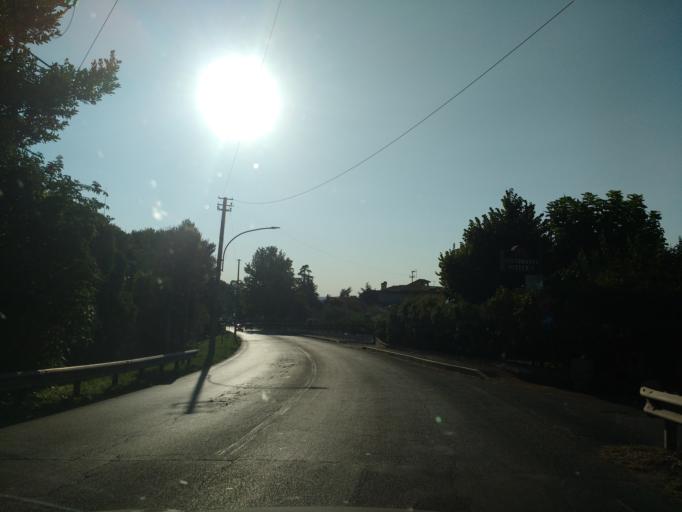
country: IT
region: Latium
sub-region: Citta metropolitana di Roma Capitale
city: Villa Adriana
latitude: 41.9564
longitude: 12.7830
